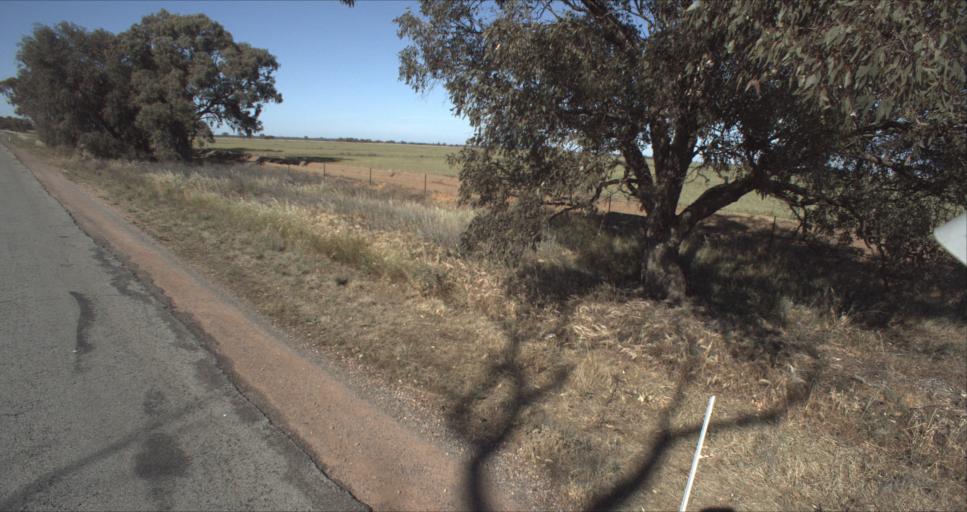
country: AU
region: New South Wales
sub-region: Leeton
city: Leeton
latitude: -34.5555
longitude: 146.3138
